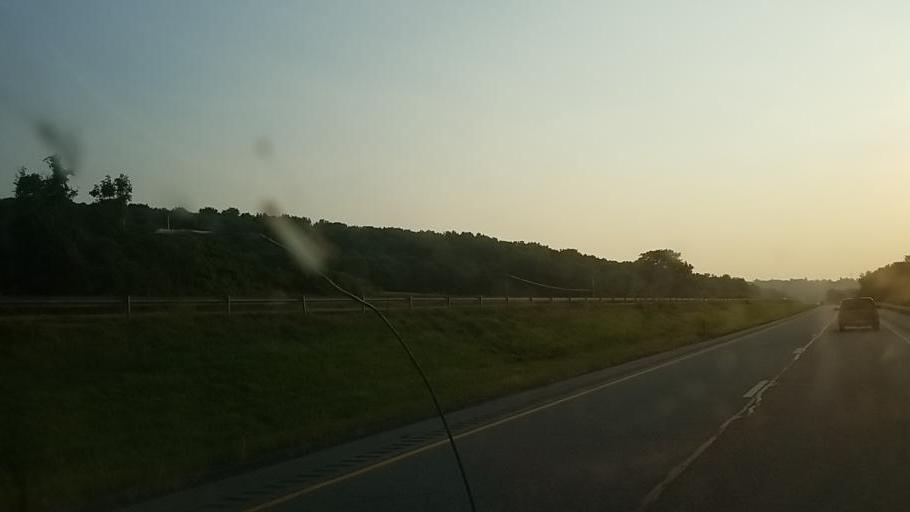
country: US
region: New York
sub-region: Montgomery County
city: Saint Johnsville
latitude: 42.9906
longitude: -74.6982
